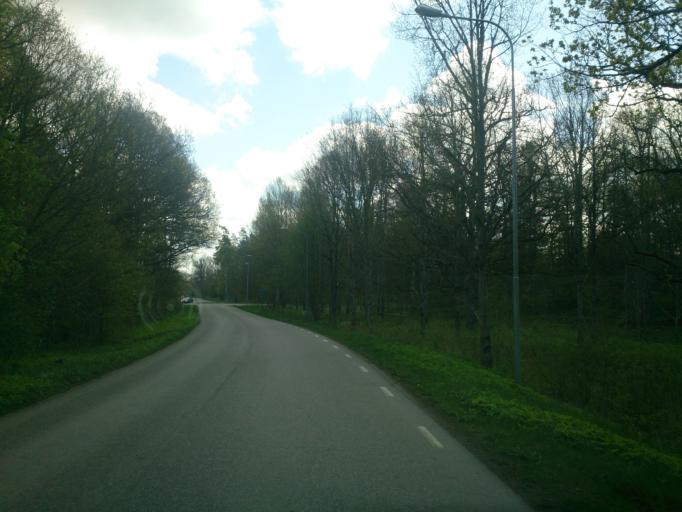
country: SE
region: OEstergoetland
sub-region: Atvidabergs Kommun
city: Atvidaberg
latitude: 58.1980
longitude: 15.9812
